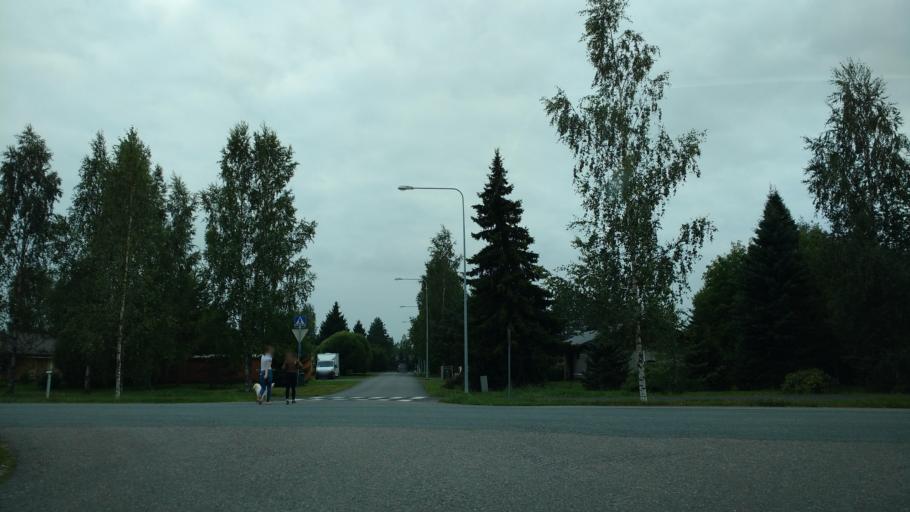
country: FI
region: Haeme
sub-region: Forssa
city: Ypaejae
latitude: 60.8068
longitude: 23.2762
